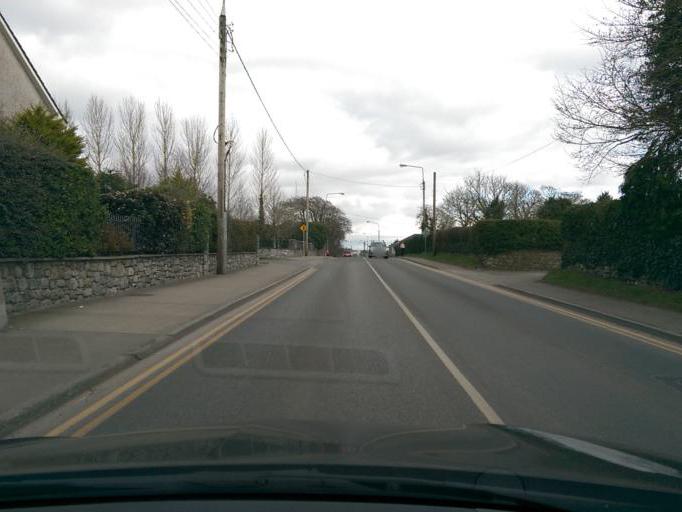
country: IE
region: Leinster
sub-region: An Iarmhi
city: Athlone
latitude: 53.4184
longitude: -7.9116
